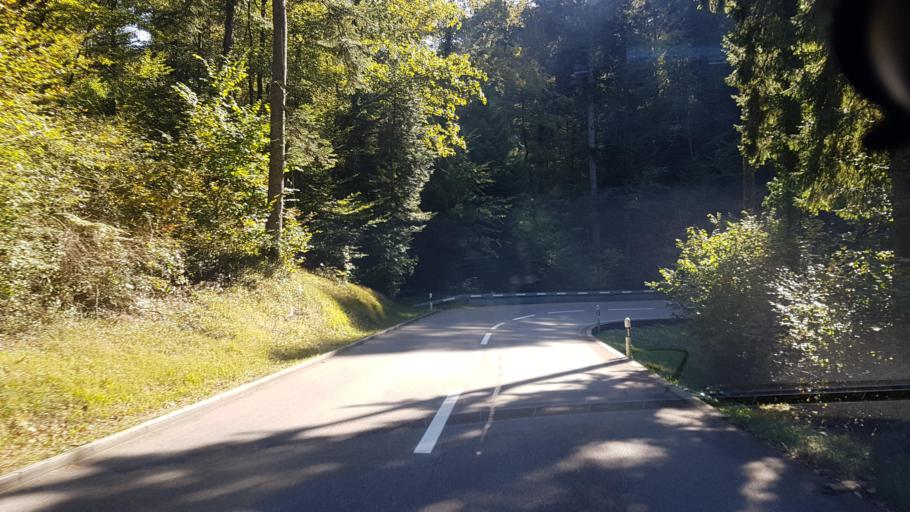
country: CH
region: Aargau
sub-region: Bezirk Laufenburg
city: Sulz
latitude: 47.5187
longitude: 8.1187
